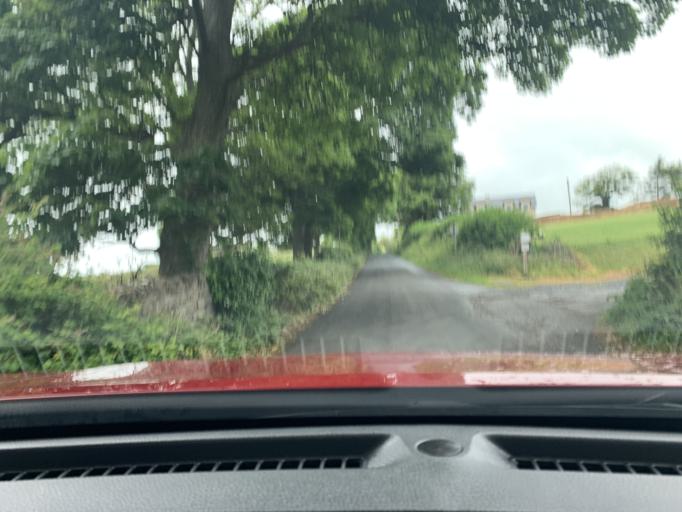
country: IE
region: Connaught
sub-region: Sligo
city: Sligo
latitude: 54.2924
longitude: -8.4634
